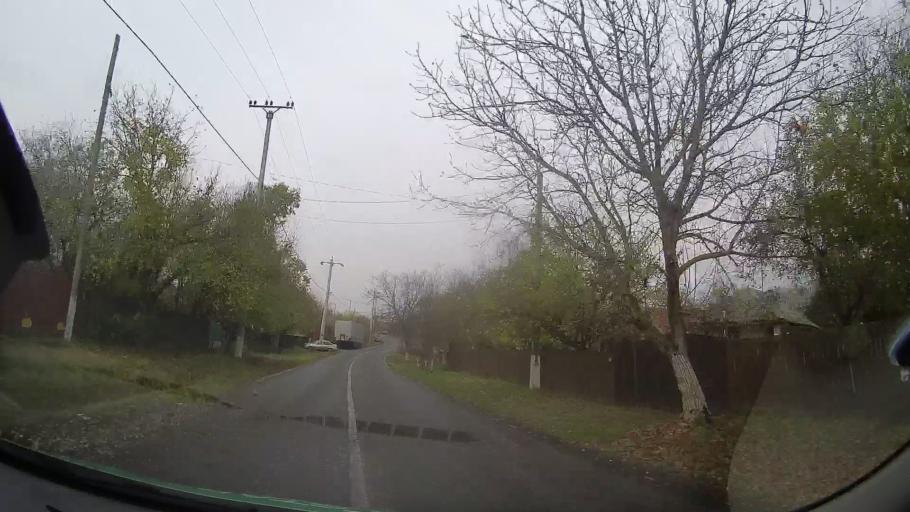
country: RO
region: Ilfov
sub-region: Comuna Gruiu
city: Gruiu
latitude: 44.7262
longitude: 26.2138
